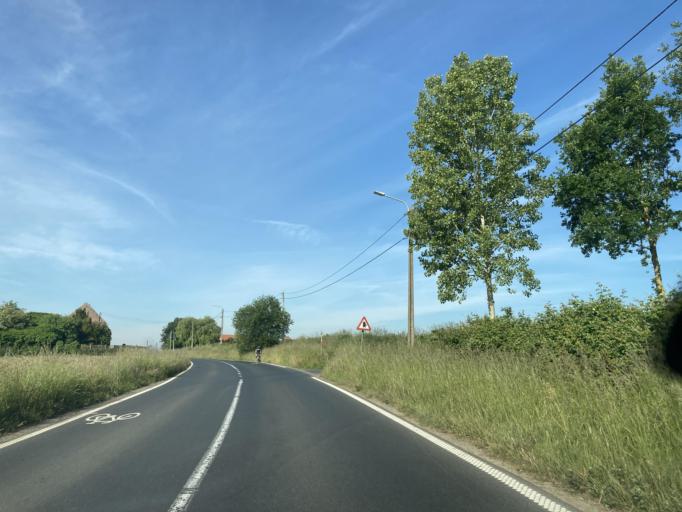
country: FR
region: Nord-Pas-de-Calais
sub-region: Departement du Nord
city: Nieppe
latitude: 50.7705
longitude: 2.8207
